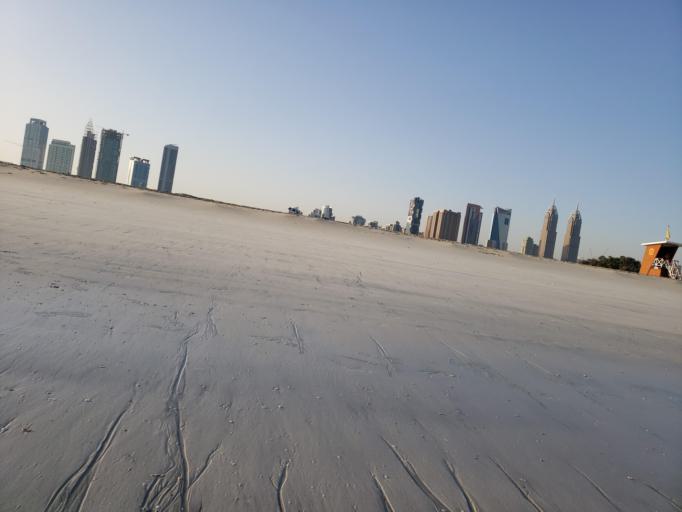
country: AE
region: Dubai
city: Dubai
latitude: 25.1174
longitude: 55.1668
